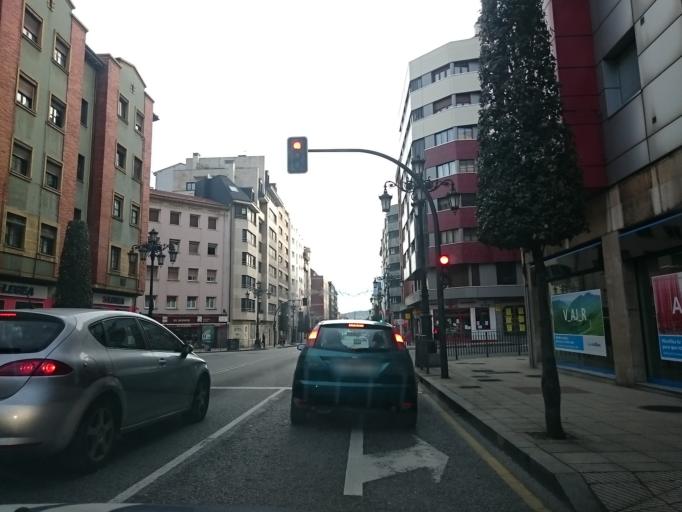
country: ES
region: Asturias
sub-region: Province of Asturias
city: Oviedo
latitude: 43.3615
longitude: -5.8388
